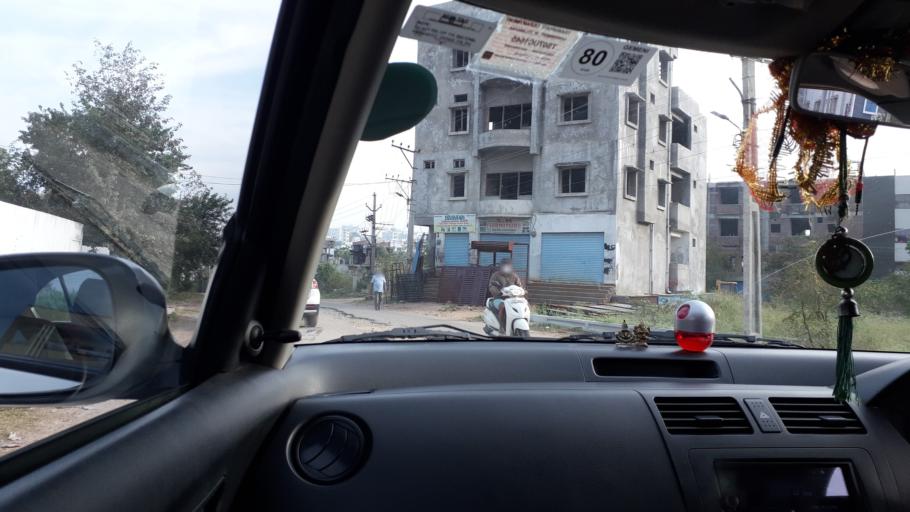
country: IN
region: Telangana
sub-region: Hyderabad
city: Hyderabad
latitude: 17.3908
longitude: 78.3842
